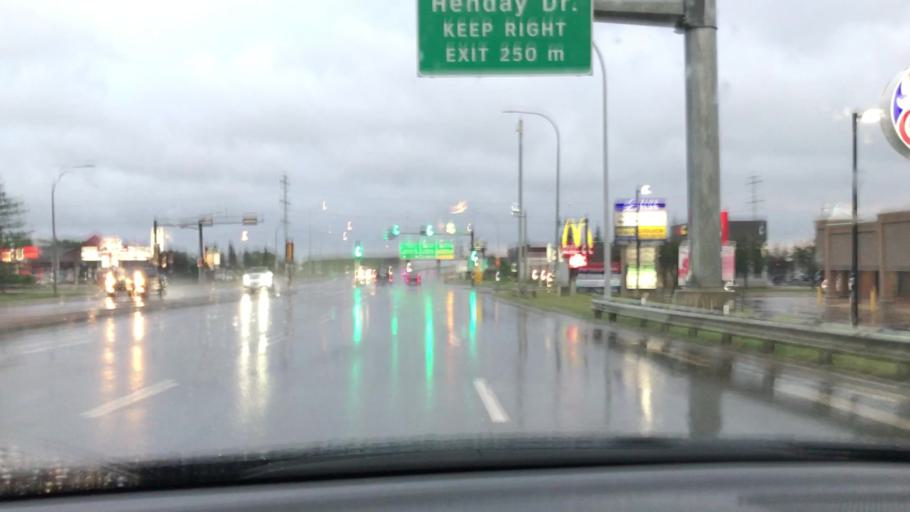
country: CA
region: Alberta
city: Sherwood Park
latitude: 53.5122
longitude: -113.3289
